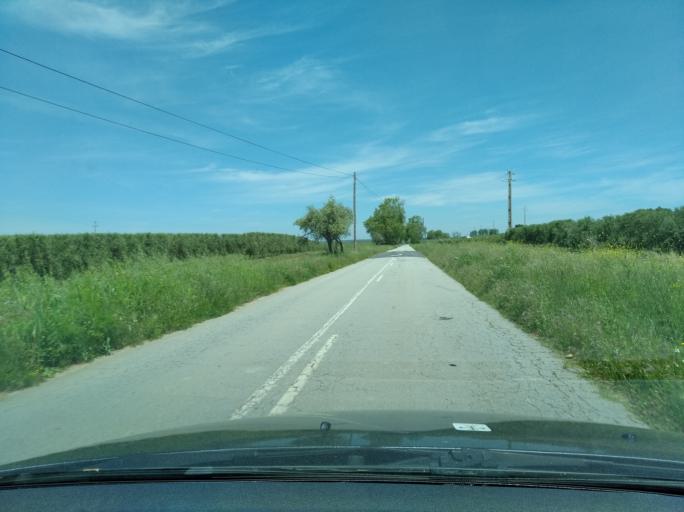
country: PT
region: Portalegre
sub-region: Avis
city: Avis
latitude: 39.0742
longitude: -7.8814
